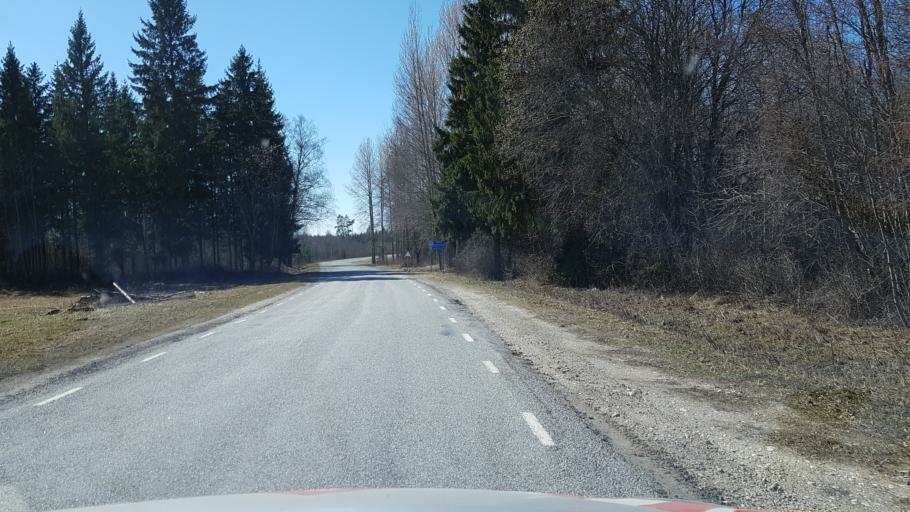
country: EE
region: Jaervamaa
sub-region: Koeru vald
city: Koeru
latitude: 59.0455
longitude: 26.0495
